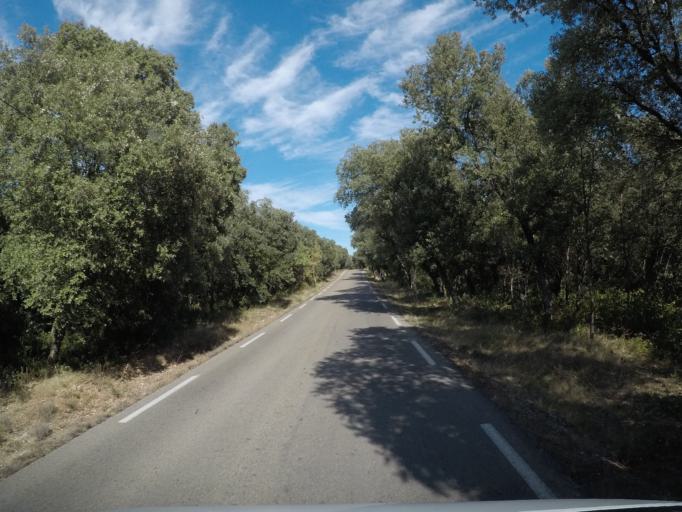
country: FR
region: Languedoc-Roussillon
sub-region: Departement du Gard
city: Sauve
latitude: 43.9960
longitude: 3.9721
